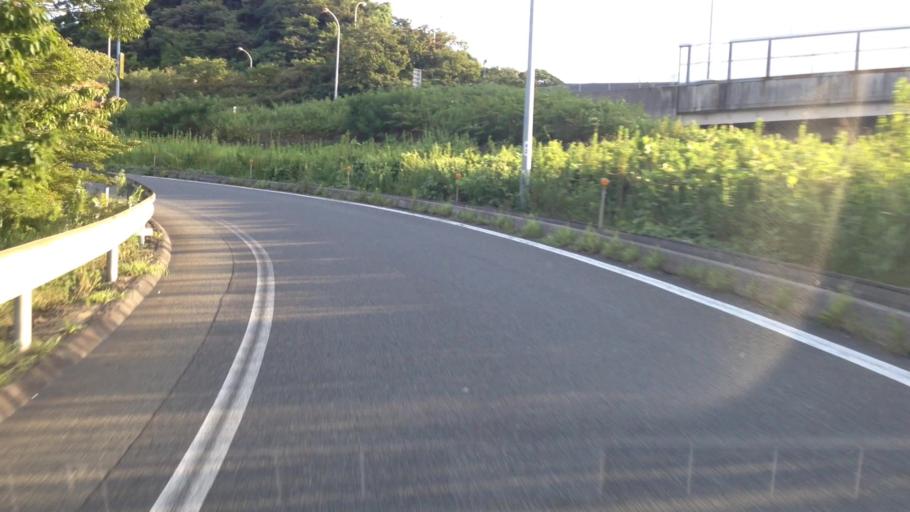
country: JP
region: Kanagawa
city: Yokosuka
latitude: 35.2429
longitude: 139.6584
